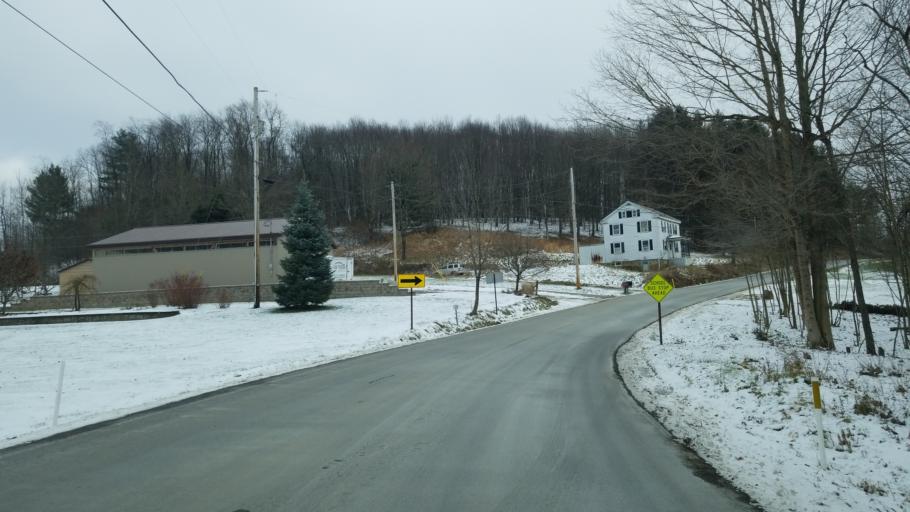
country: US
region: Pennsylvania
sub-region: Clearfield County
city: Sandy
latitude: 41.0954
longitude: -78.7543
